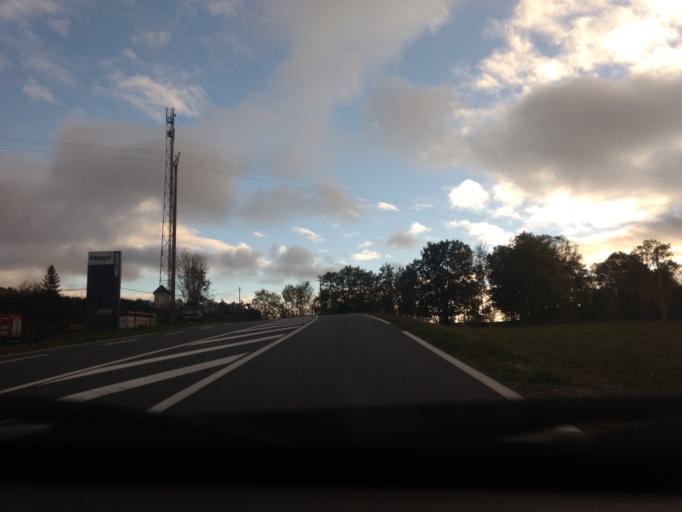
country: FR
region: Midi-Pyrenees
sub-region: Departement de l'Aveyron
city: Laguiole
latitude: 44.6743
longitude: 2.8505
